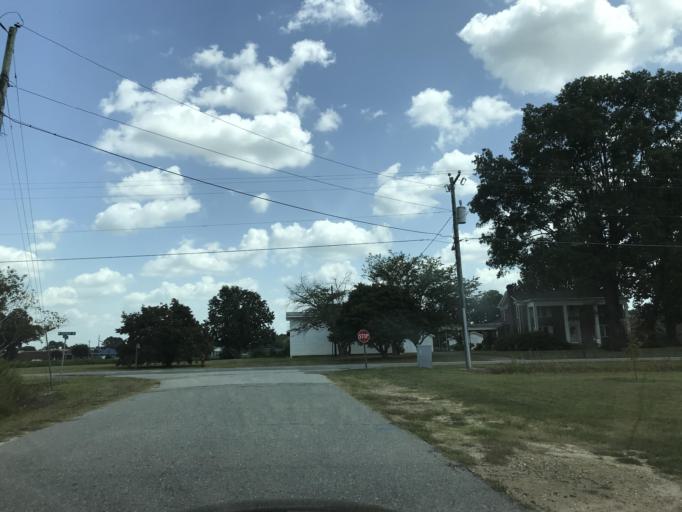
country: US
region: North Carolina
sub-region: Sampson County
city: Plain View
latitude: 35.2477
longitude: -78.3589
